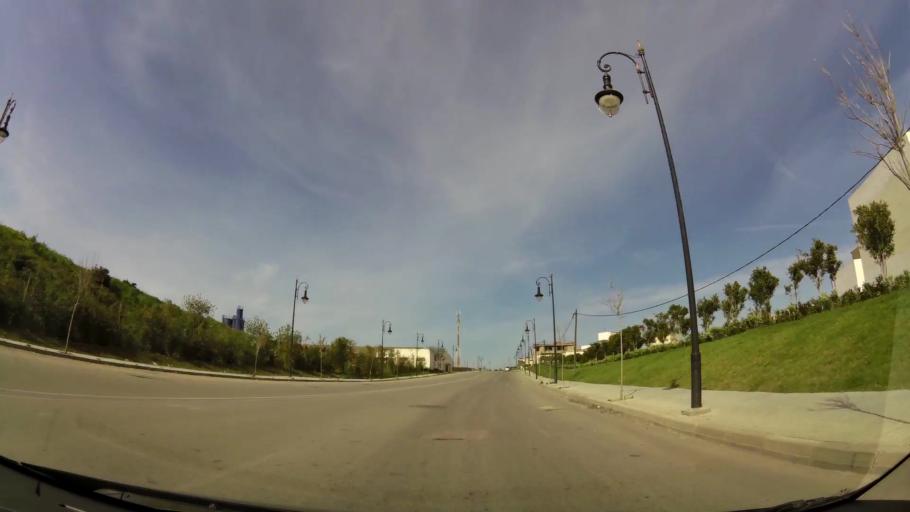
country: MA
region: Tanger-Tetouan
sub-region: Tanger-Assilah
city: Tangier
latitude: 35.7087
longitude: -5.8064
